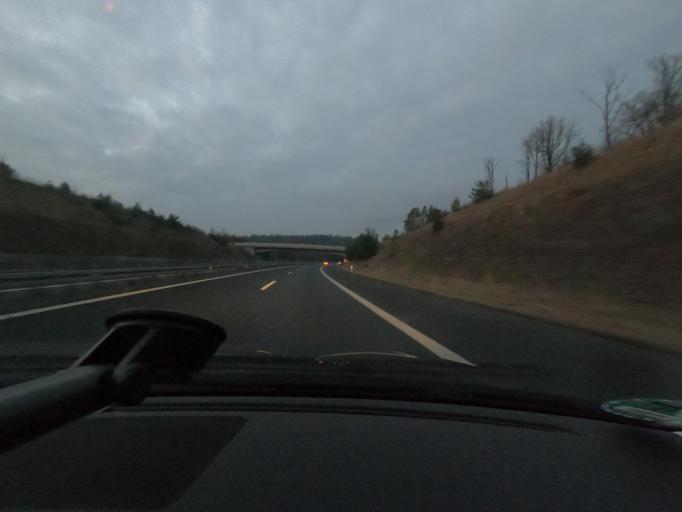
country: DE
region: Bavaria
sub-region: Upper Franconia
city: Untersiemau
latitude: 50.1652
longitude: 11.0084
